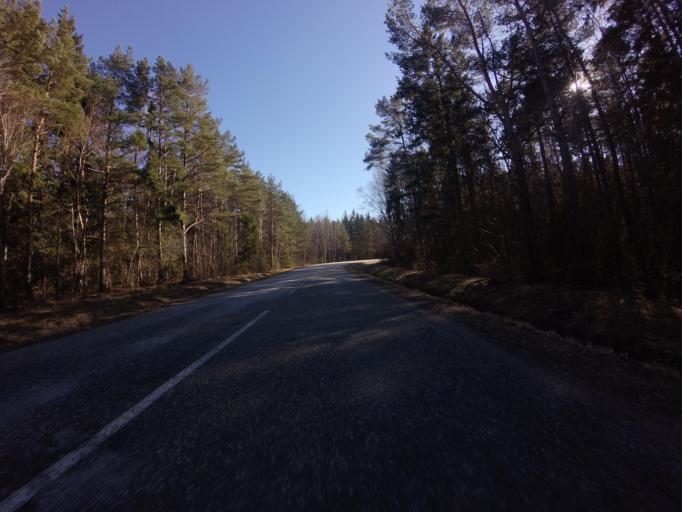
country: EE
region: Saare
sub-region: Kuressaare linn
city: Kuressaare
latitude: 58.5707
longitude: 22.4219
